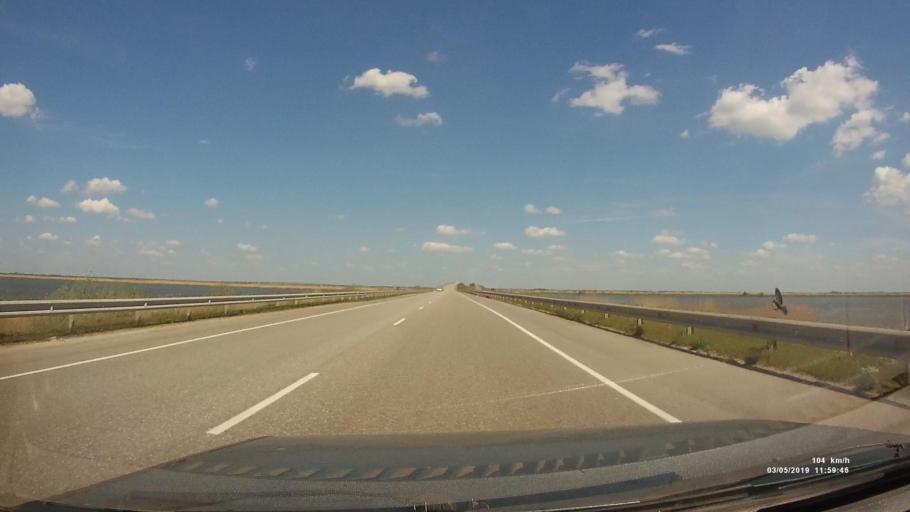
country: RU
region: Rostov
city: Bagayevskaya
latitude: 47.2395
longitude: 40.3336
